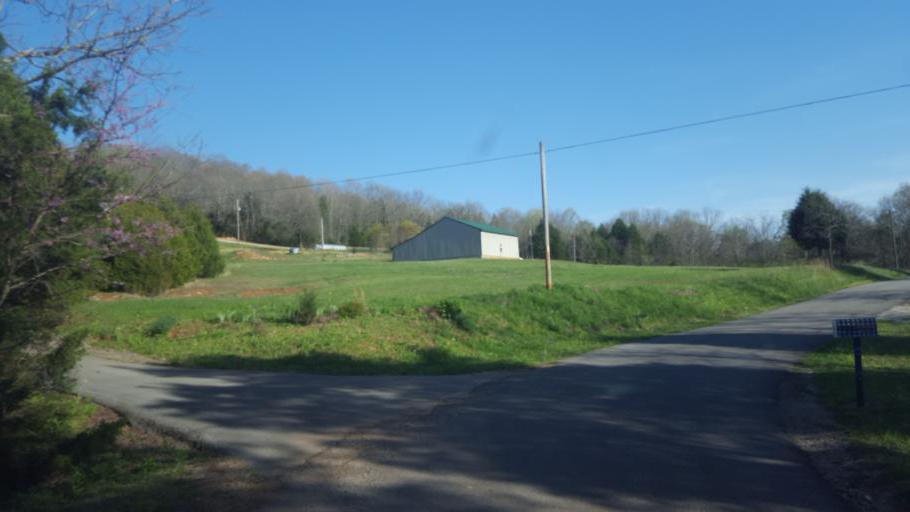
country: US
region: Kentucky
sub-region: Barren County
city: Cave City
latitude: 37.1966
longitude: -86.0118
